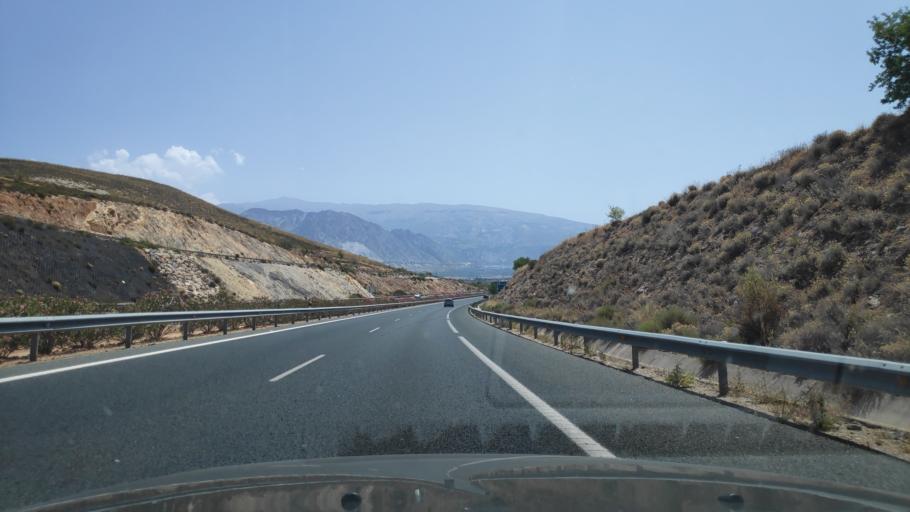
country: ES
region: Andalusia
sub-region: Provincia de Granada
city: Padul
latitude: 36.9911
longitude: -3.6183
